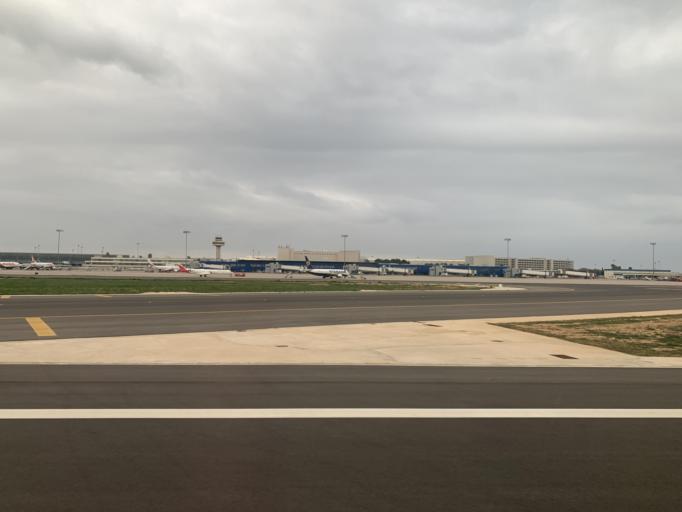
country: ES
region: Balearic Islands
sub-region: Illes Balears
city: s'Arenal
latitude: 39.5551
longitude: 2.7253
